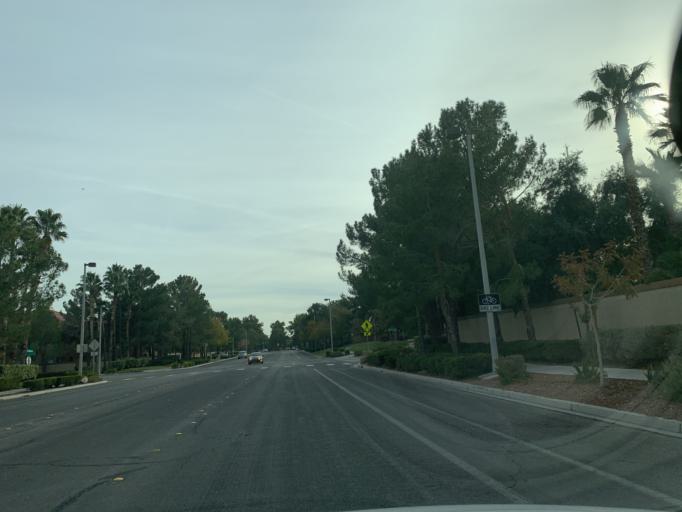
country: US
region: Nevada
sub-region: Clark County
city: Summerlin South
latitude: 36.1476
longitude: -115.3069
